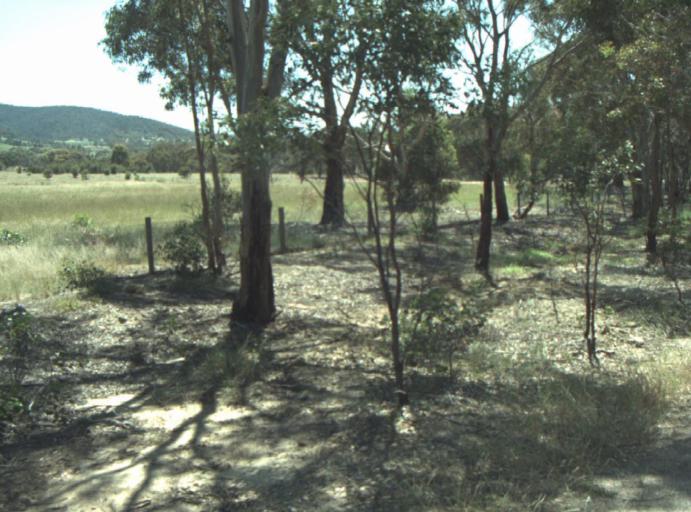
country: AU
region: Victoria
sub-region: Greater Geelong
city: Lara
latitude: -37.8381
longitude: 144.2861
